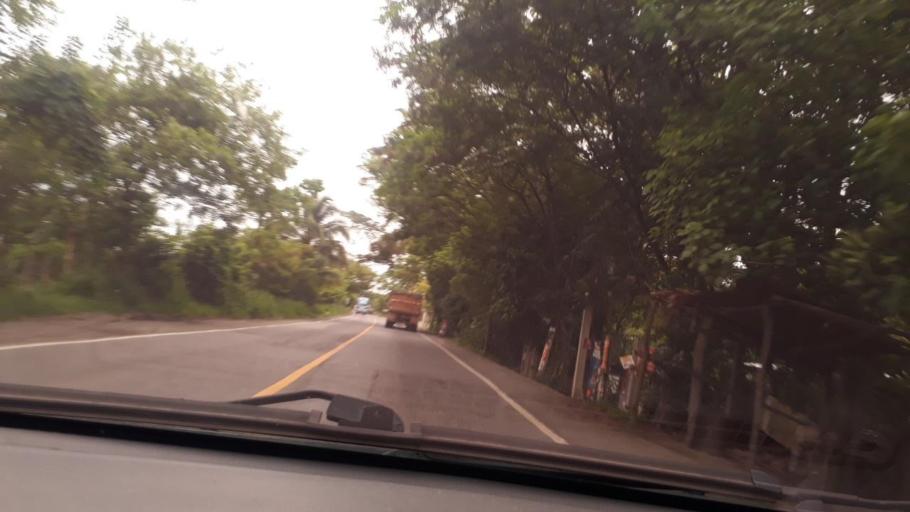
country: GT
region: Izabal
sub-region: Municipio de Los Amates
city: Los Amates
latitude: 15.3087
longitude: -89.0553
